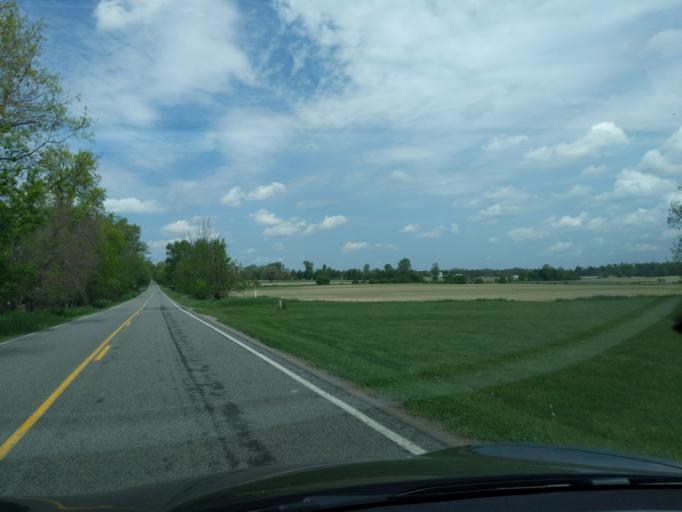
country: US
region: Michigan
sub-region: Ingham County
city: Stockbridge
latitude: 42.4930
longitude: -84.1601
